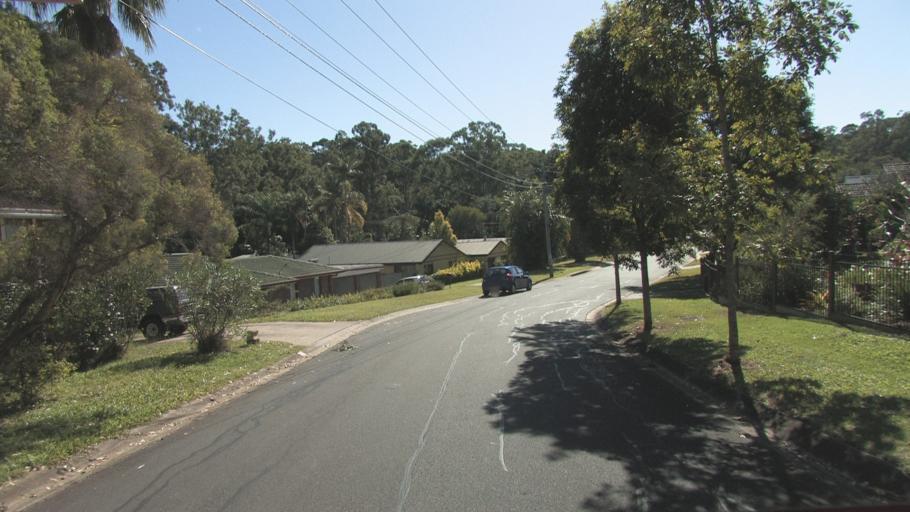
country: AU
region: Queensland
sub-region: Logan
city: Slacks Creek
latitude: -27.6390
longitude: 153.1611
